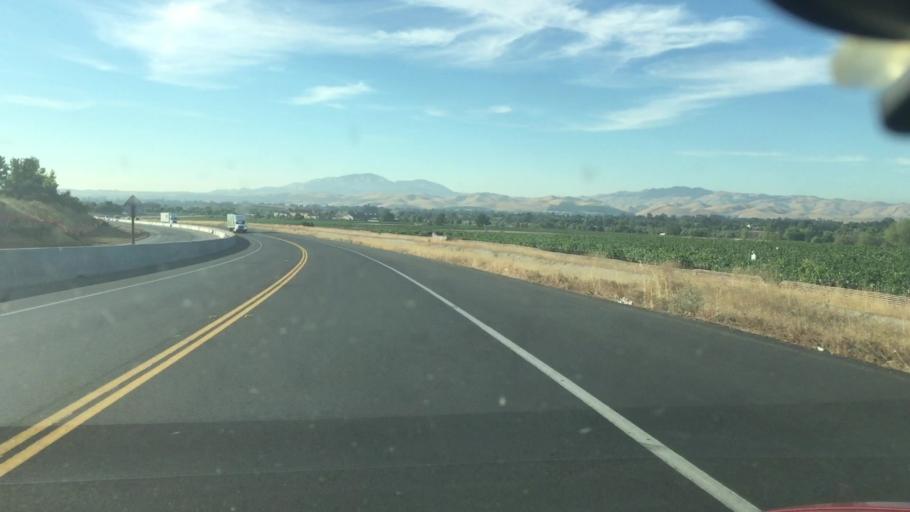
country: US
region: California
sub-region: Alameda County
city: Livermore
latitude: 37.6397
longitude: -121.8076
